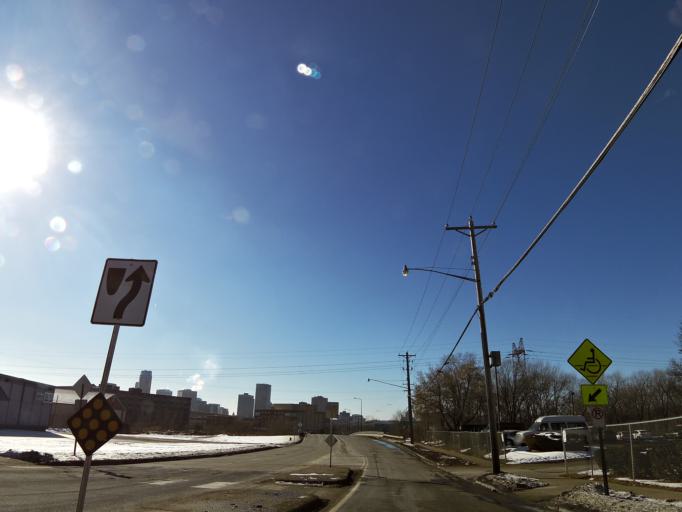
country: US
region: Minnesota
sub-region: Ramsey County
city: Saint Paul
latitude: 44.9600
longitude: -93.0820
